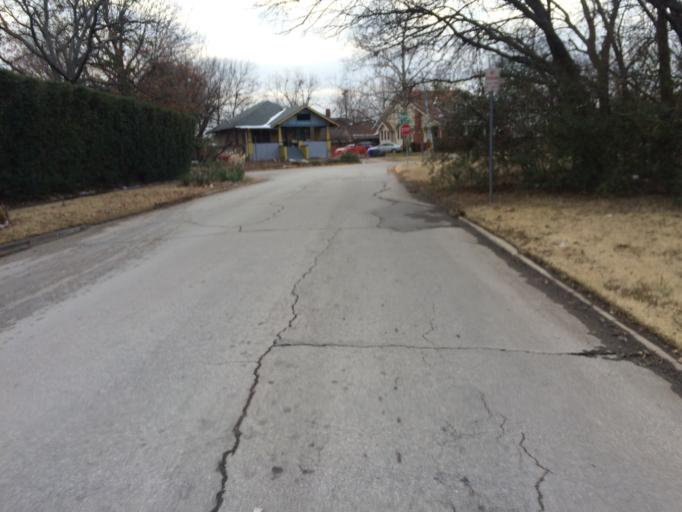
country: US
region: Oklahoma
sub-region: Cleveland County
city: Norman
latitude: 35.2184
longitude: -97.4393
